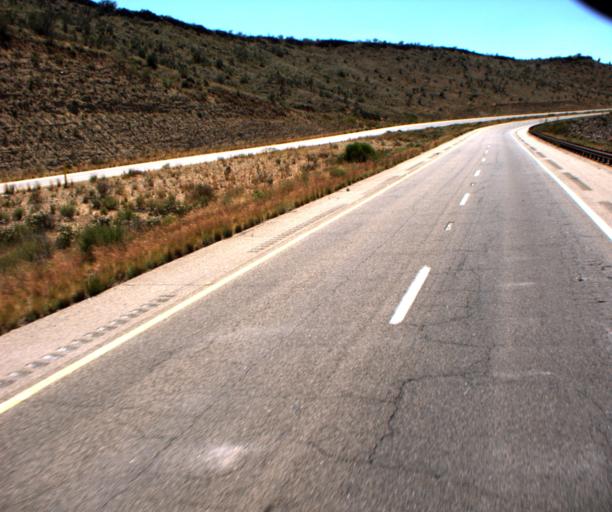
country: US
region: Arizona
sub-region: Yavapai County
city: Bagdad
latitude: 34.4480
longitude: -113.2788
